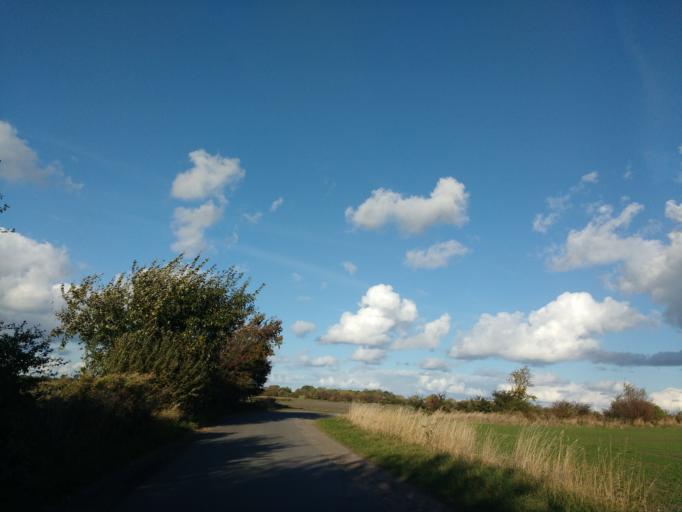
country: DE
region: Schleswig-Holstein
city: Grossenbrode
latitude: 54.4300
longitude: 11.1126
